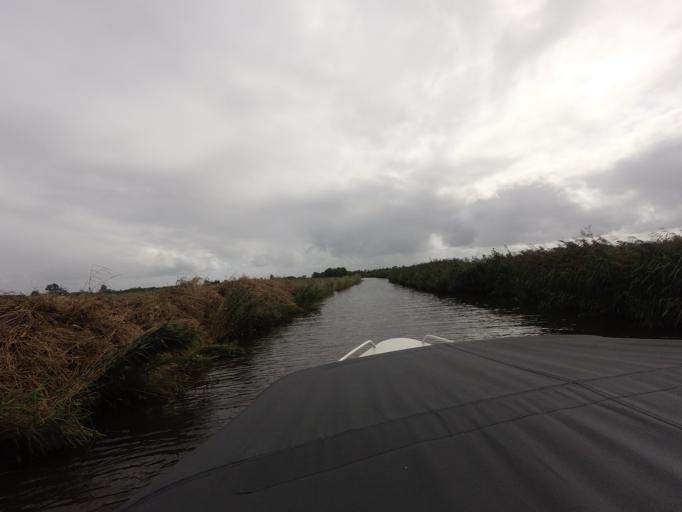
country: NL
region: Friesland
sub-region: Gemeente Boarnsterhim
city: Warten
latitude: 53.1289
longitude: 5.8992
